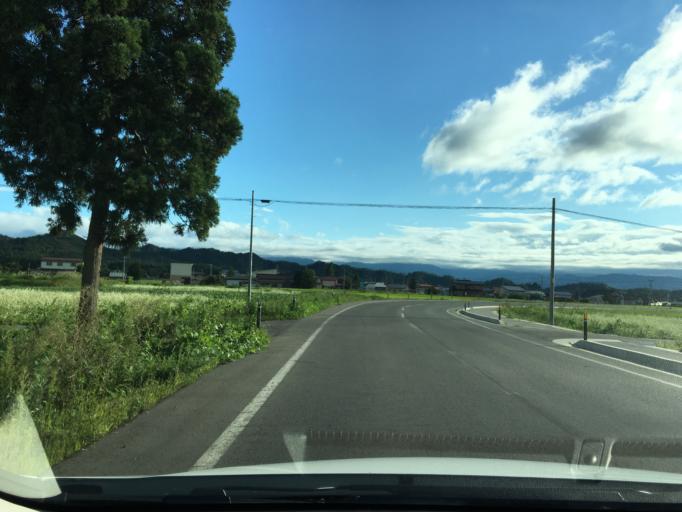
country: JP
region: Yamagata
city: Takahata
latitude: 37.9546
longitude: 140.1810
